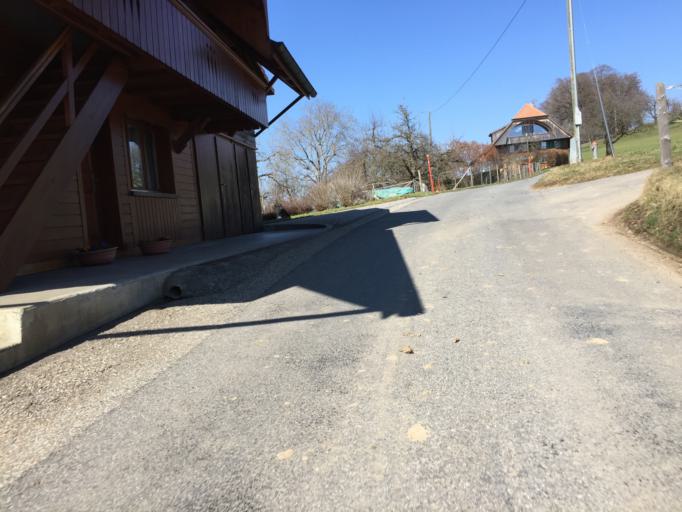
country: CH
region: Bern
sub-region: Bern-Mittelland District
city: Taegertschi
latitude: 46.8938
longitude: 7.5827
